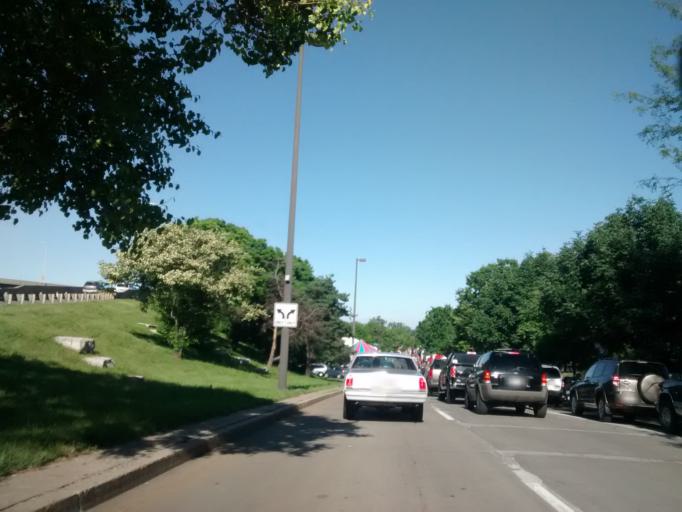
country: US
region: Nebraska
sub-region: Douglas County
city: Omaha
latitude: 41.2586
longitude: -95.9276
